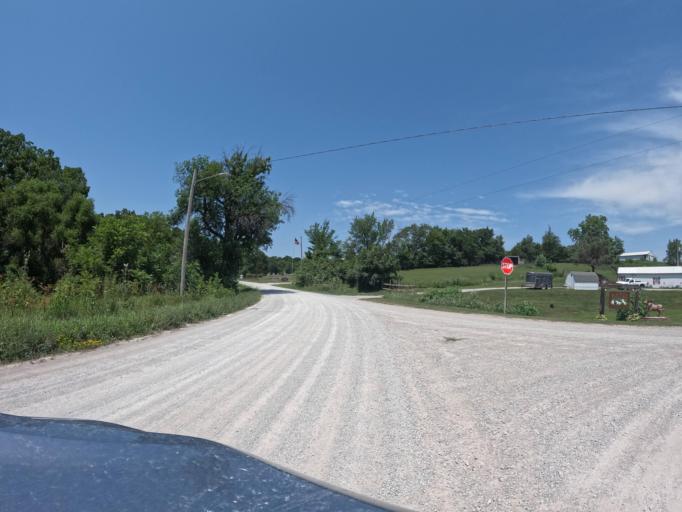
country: US
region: Iowa
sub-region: Appanoose County
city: Centerville
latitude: 40.7791
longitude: -92.9572
